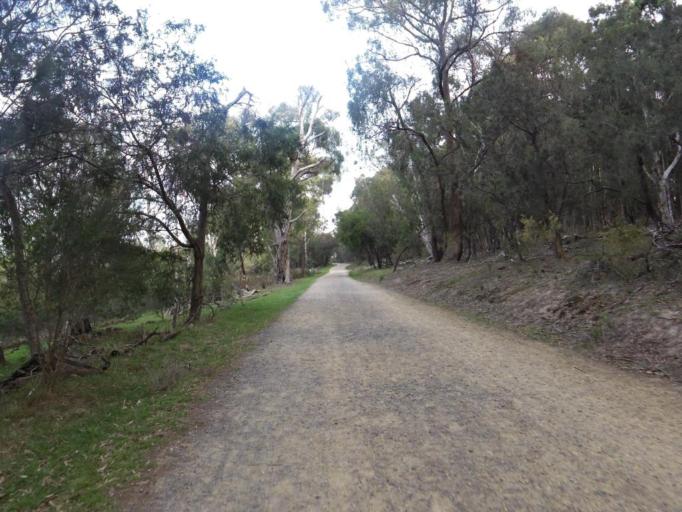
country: AU
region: Victoria
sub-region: Casey
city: Narre Warren North
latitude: -37.9683
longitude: 145.2928
